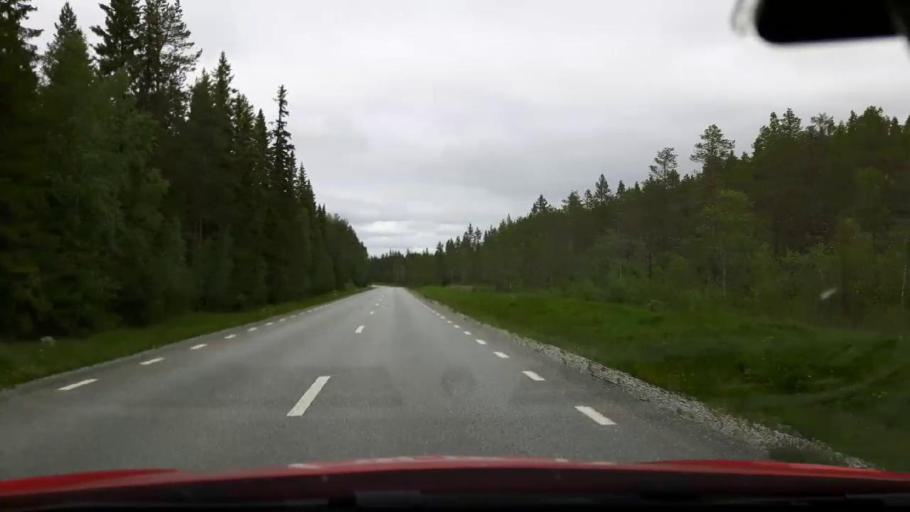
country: SE
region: Jaemtland
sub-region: OEstersunds Kommun
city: Lit
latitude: 63.6950
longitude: 14.6837
